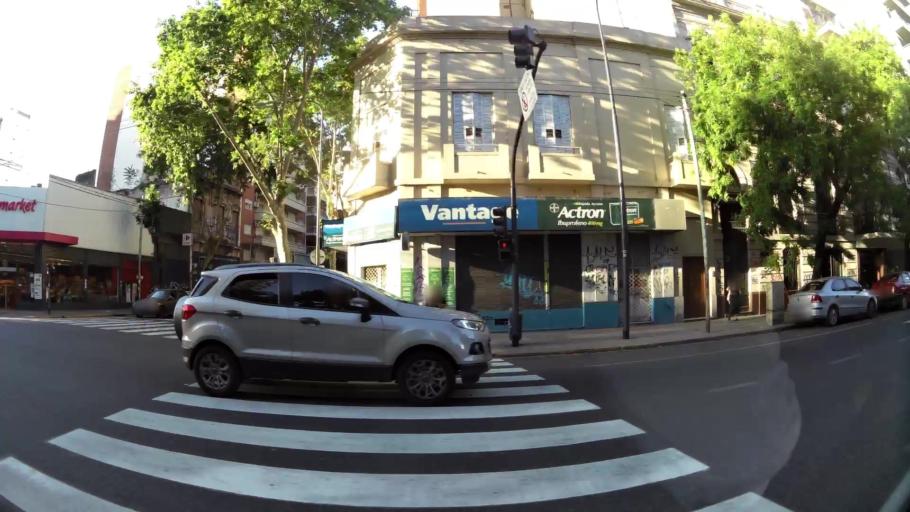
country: AR
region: Buenos Aires F.D.
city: Buenos Aires
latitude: -34.6086
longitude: -58.4213
